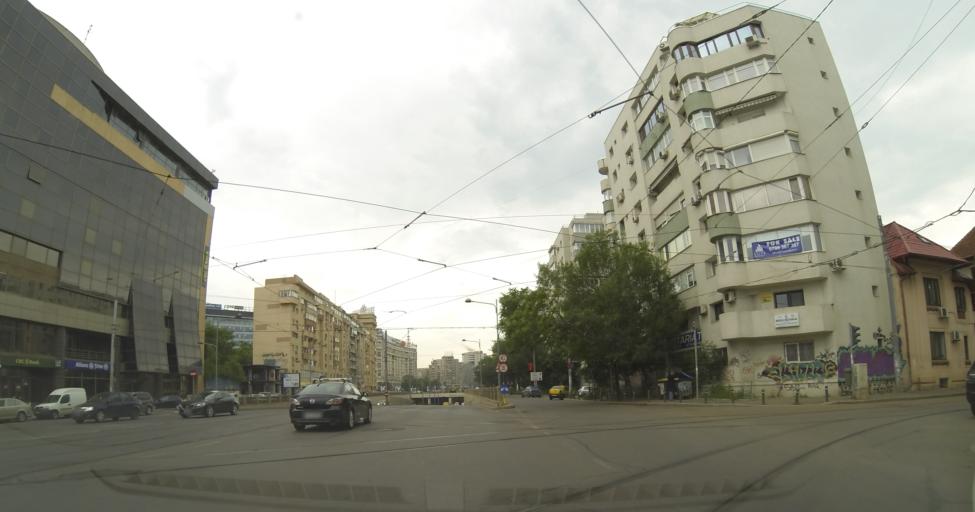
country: RO
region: Bucuresti
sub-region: Municipiul Bucuresti
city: Bucuresti
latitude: 44.4526
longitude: 26.0905
